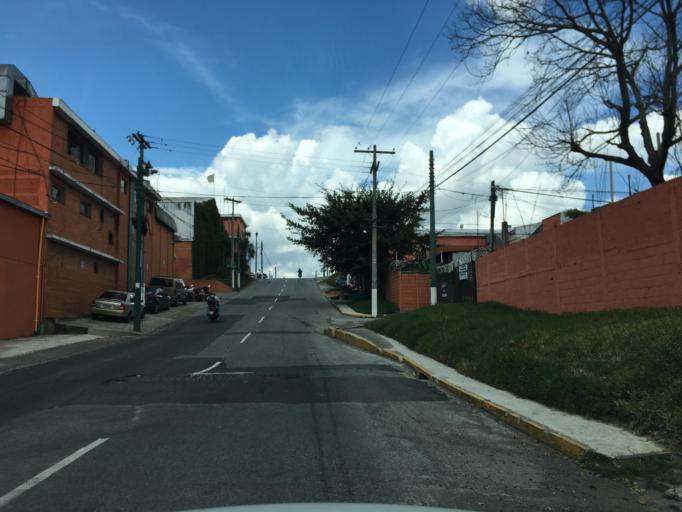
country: GT
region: Guatemala
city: Santa Catarina Pinula
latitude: 14.5898
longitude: -90.5480
